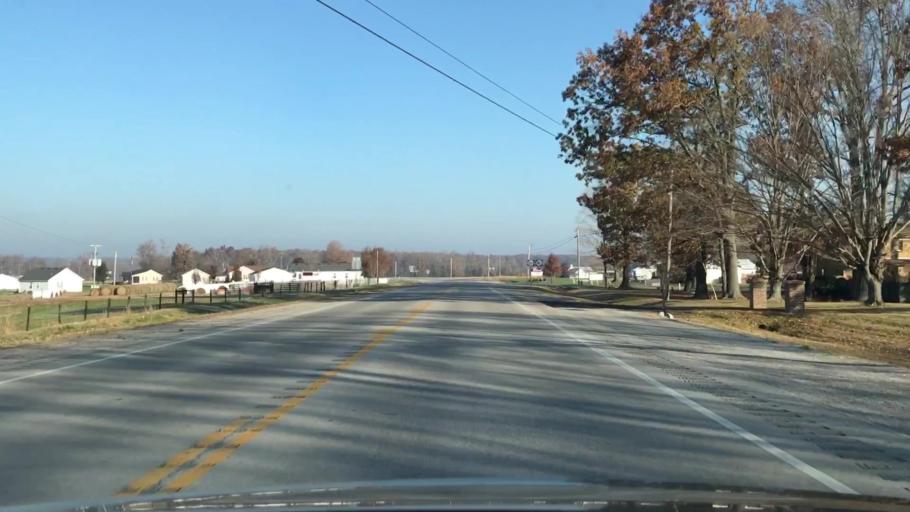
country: US
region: Kentucky
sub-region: Edmonson County
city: Brownsville
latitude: 37.1125
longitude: -86.2292
